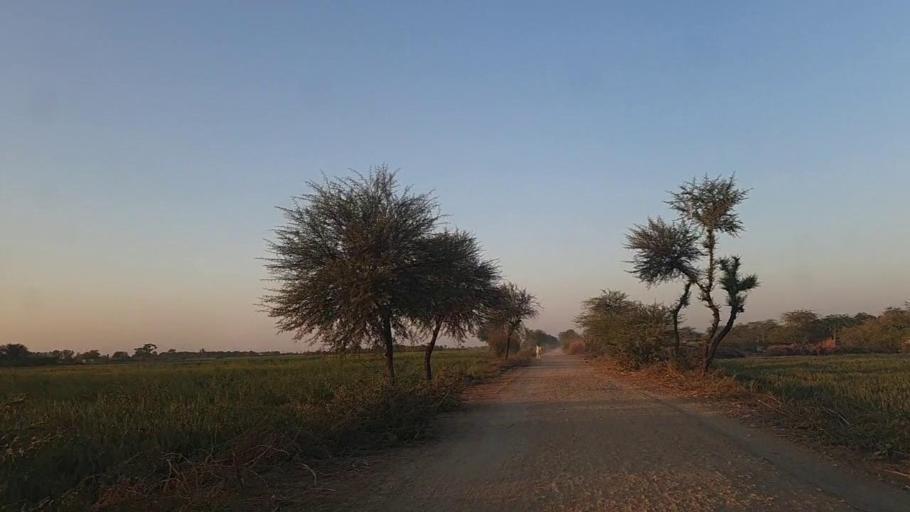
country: PK
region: Sindh
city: Naukot
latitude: 25.0508
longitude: 69.4070
